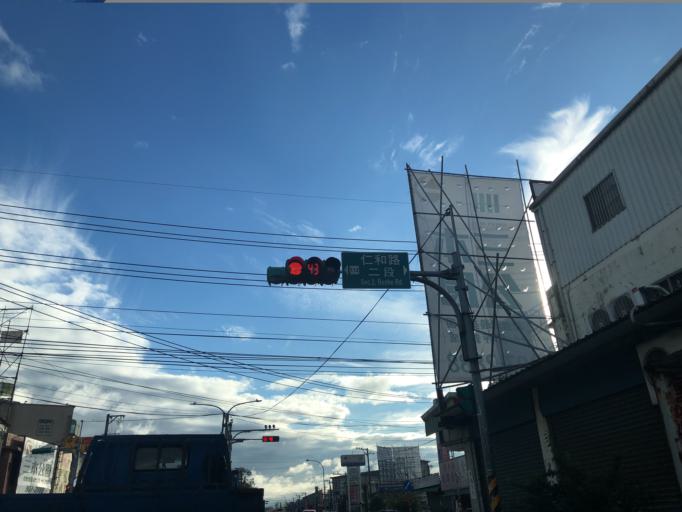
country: TW
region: Taiwan
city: Daxi
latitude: 24.9039
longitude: 121.2653
